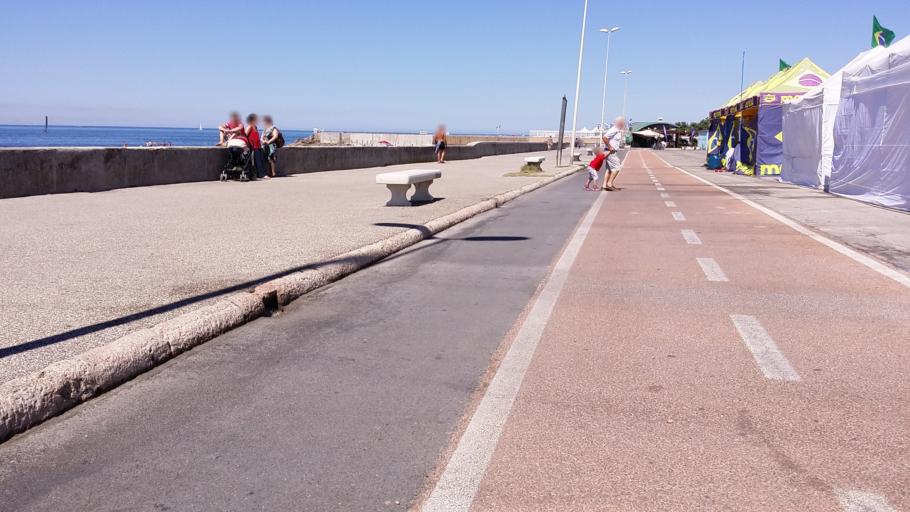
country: IT
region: Tuscany
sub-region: Provincia di Livorno
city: Livorno
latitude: 43.5125
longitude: 10.3169
